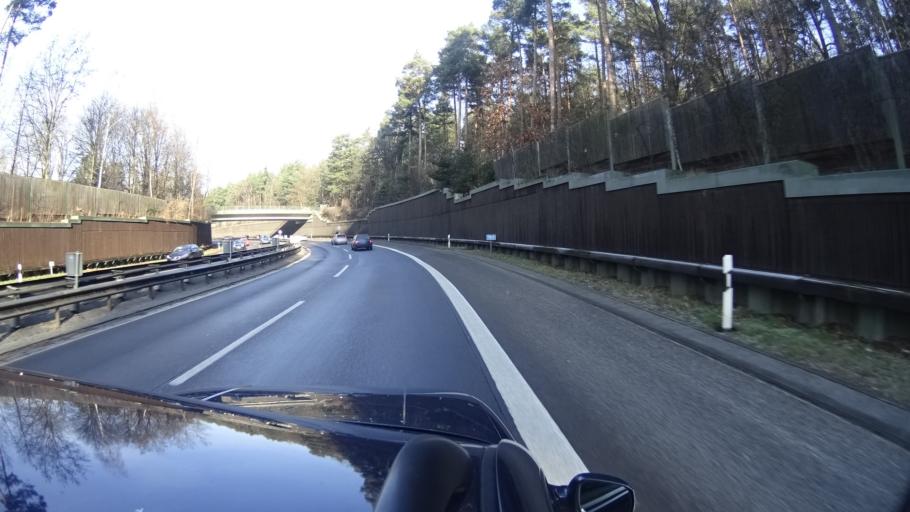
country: DE
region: Berlin
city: Heiligensee
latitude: 52.6216
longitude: 13.2489
